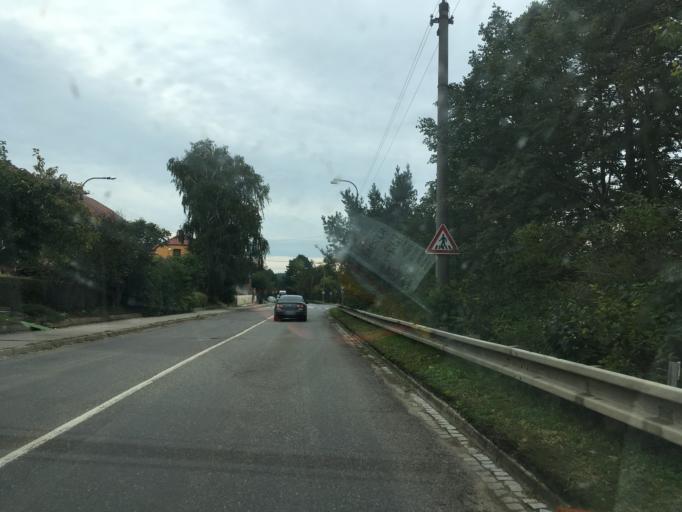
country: CZ
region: South Moravian
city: Ivancice
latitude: 49.1014
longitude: 16.3870
